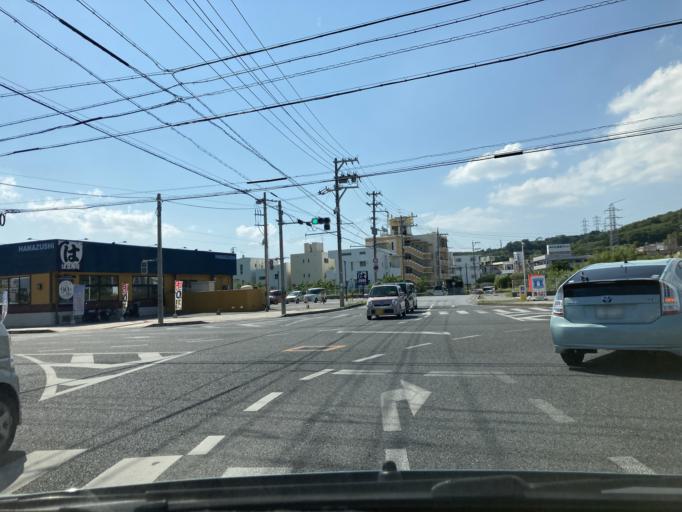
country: JP
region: Okinawa
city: Tomigusuku
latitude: 26.1879
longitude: 127.7102
